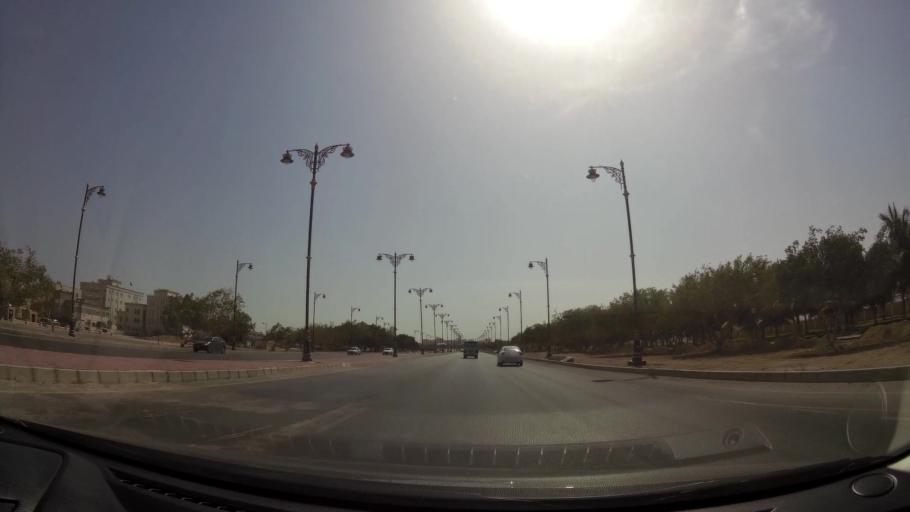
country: OM
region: Zufar
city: Salalah
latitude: 17.0233
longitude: 54.0770
